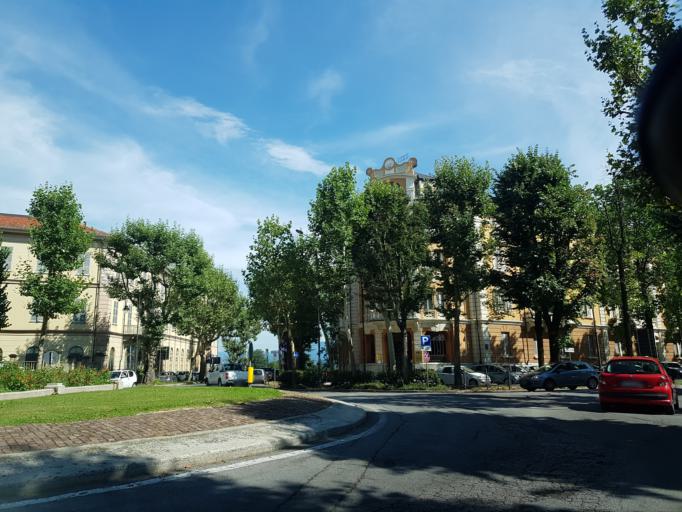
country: IT
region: Piedmont
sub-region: Provincia di Cuneo
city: Cuneo
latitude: 44.3879
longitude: 7.5487
